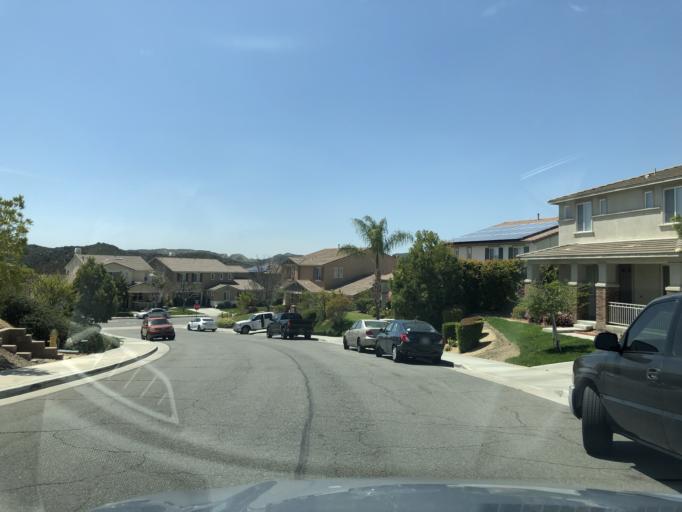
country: US
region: California
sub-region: Riverside County
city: Calimesa
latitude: 33.9627
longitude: -117.0522
